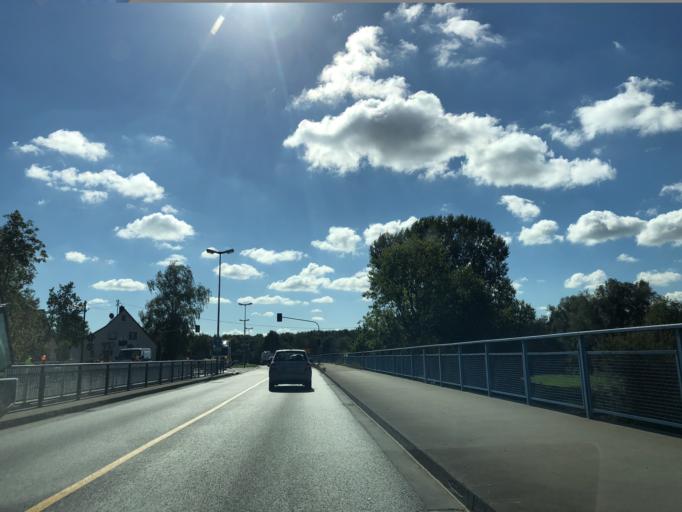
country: DE
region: Baden-Wuerttemberg
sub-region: Tuebingen Region
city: Ulm
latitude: 48.3615
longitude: 9.9629
